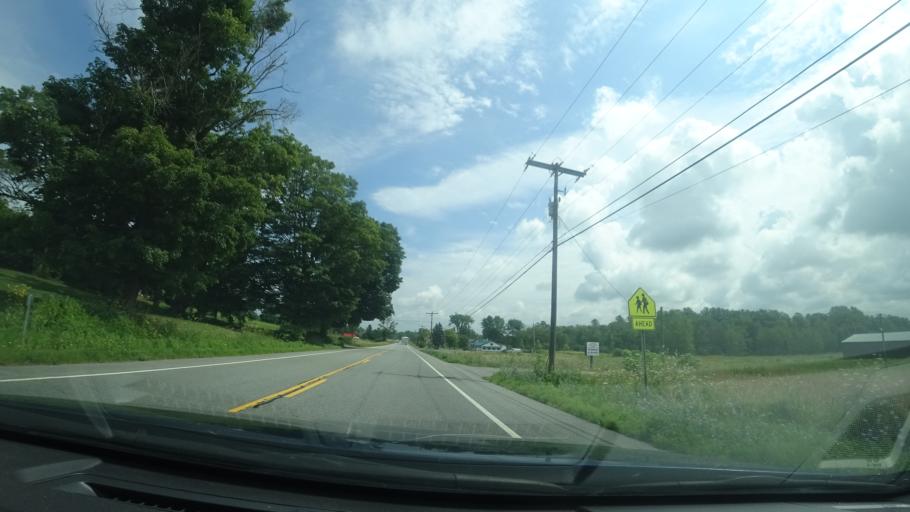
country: US
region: New York
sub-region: Warren County
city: Queensbury
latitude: 43.3680
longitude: -73.5242
